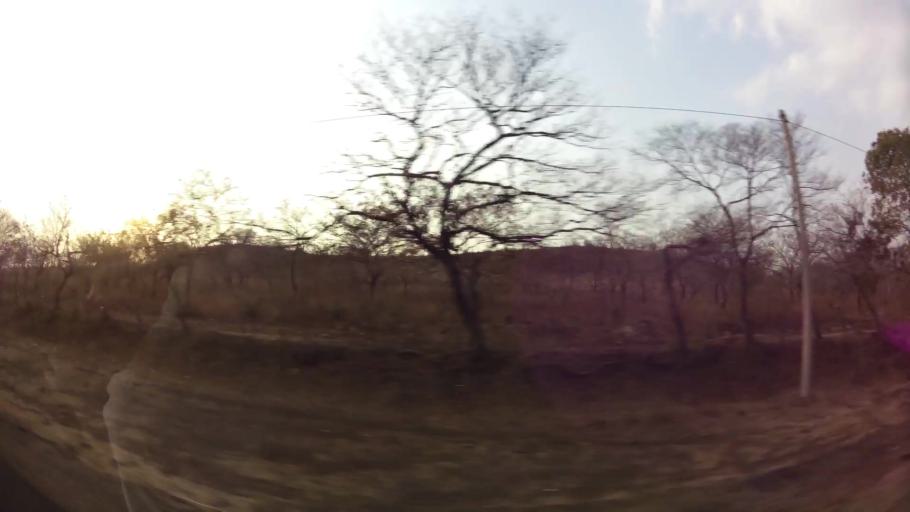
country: NI
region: Leon
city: Nagarote
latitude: 12.2704
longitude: -86.5382
